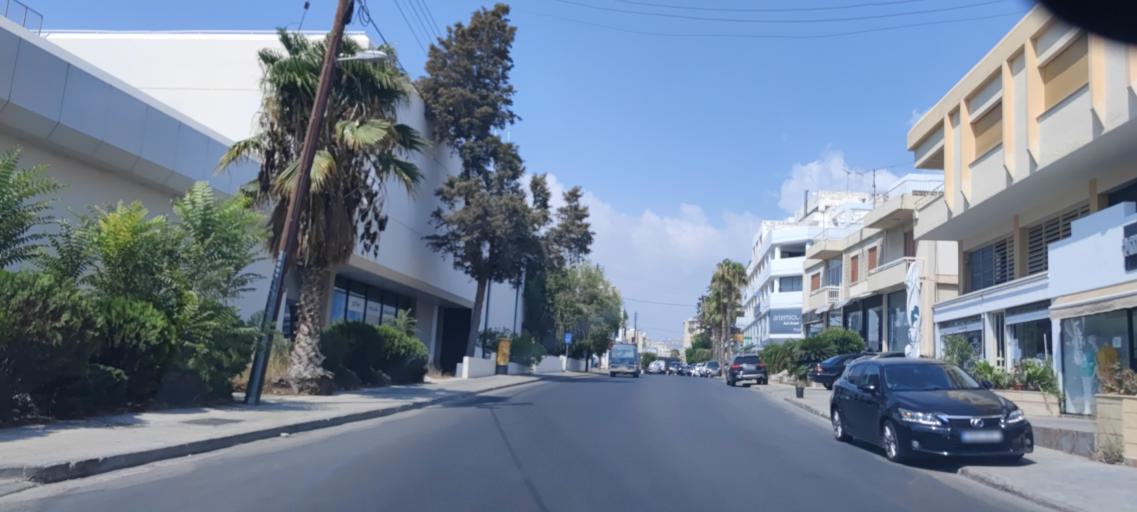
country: CY
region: Limassol
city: Limassol
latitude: 34.6860
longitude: 33.0320
